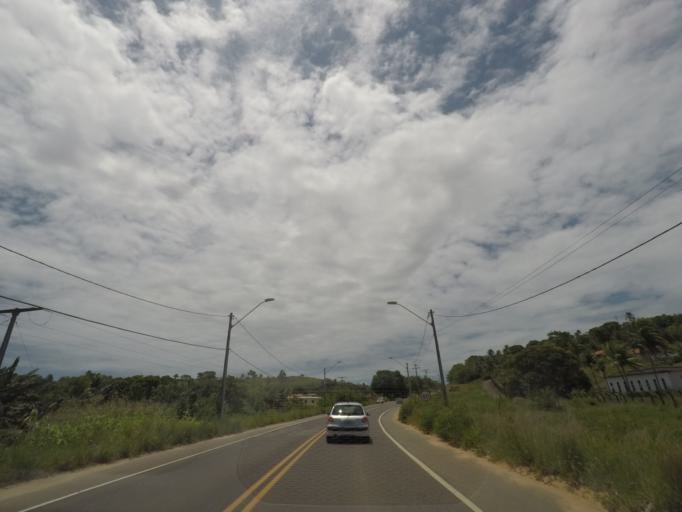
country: BR
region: Bahia
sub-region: Itaparica
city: Itaparica
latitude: -12.9369
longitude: -38.6253
